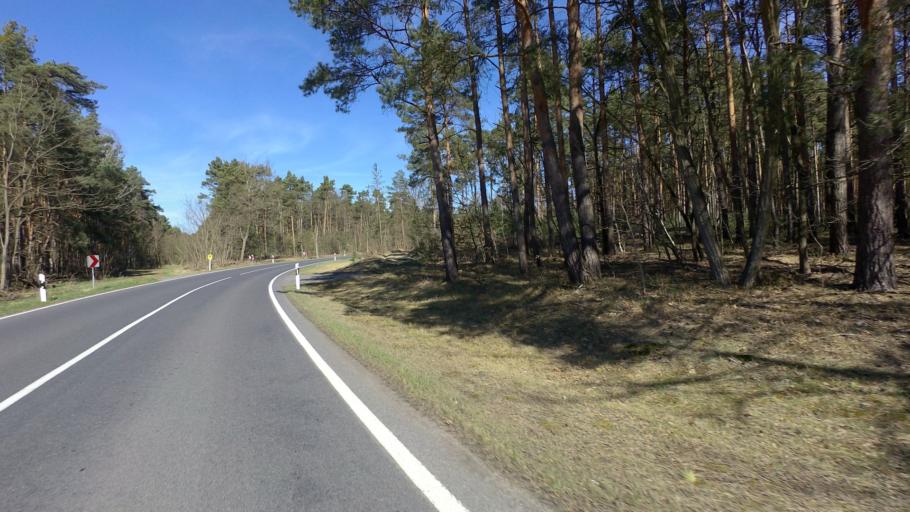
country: DE
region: Brandenburg
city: Storkow
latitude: 52.2029
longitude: 13.9241
